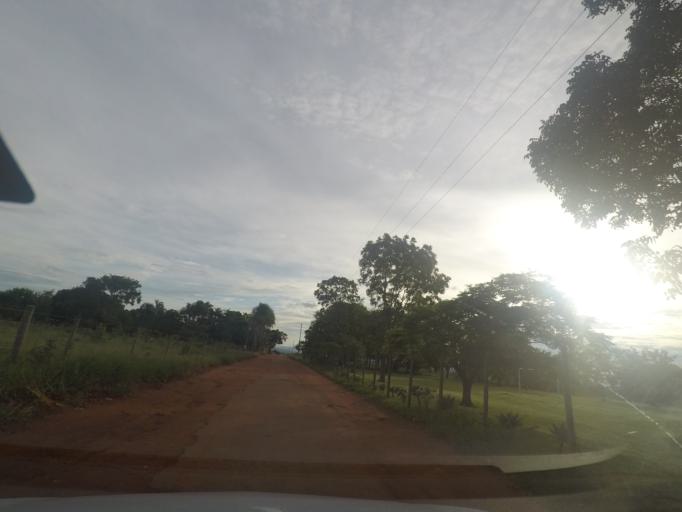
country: BR
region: Goias
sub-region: Trindade
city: Trindade
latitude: -16.7333
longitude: -49.4152
